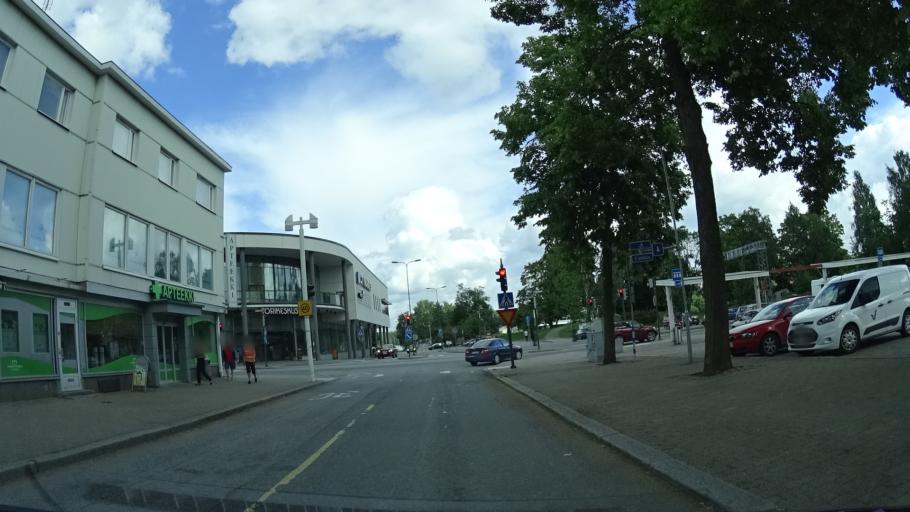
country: FI
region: Pirkanmaa
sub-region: Etelae-Pirkanmaa
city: Valkeakoski
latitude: 61.2669
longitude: 24.0305
